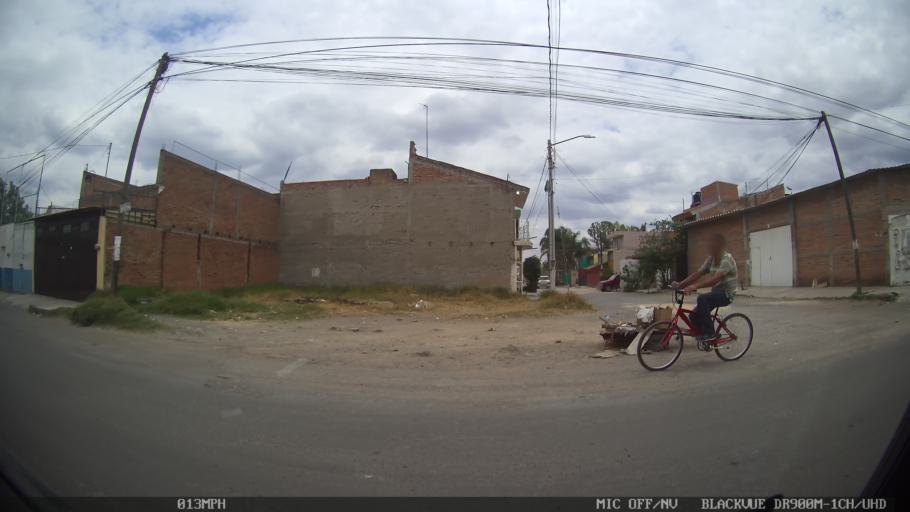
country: MX
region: Jalisco
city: Tlaquepaque
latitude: 20.6458
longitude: -103.2710
